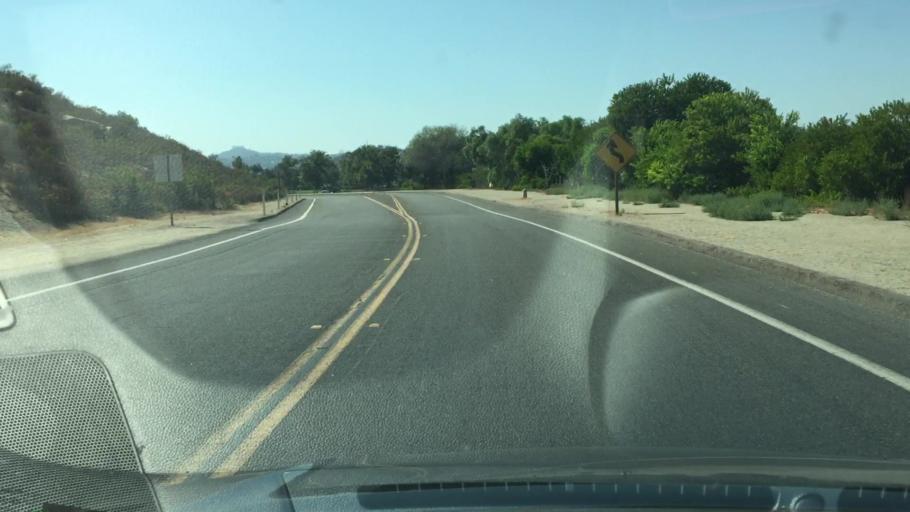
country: US
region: California
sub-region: San Diego County
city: Jamul
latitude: 32.7384
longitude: -116.8946
